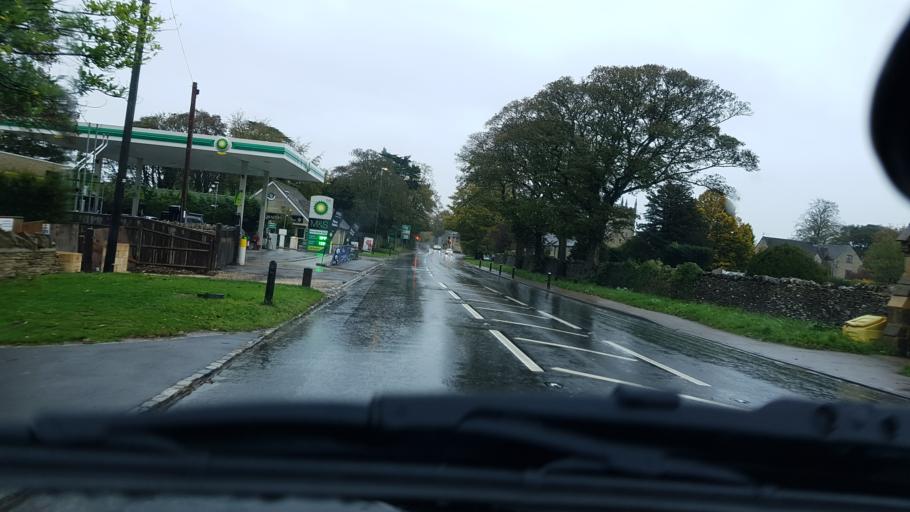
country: GB
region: England
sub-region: Gloucestershire
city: Stow on the Wold
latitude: 51.9275
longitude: -1.7255
